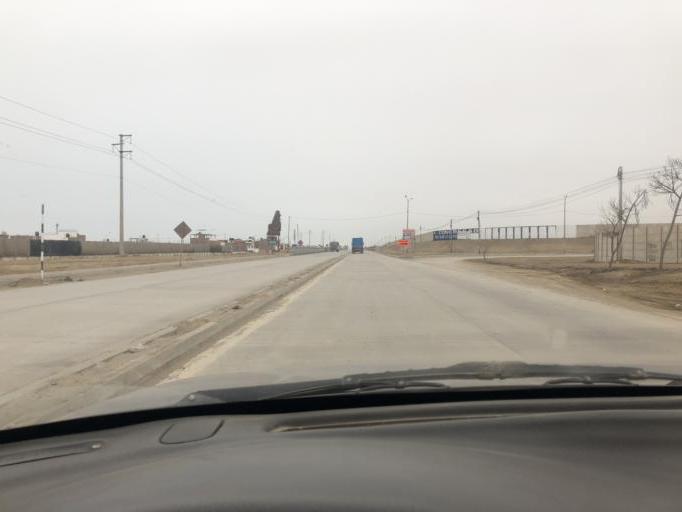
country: PE
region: Lima
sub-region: Lima
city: San Bartolo
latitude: -12.3768
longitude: -76.7825
